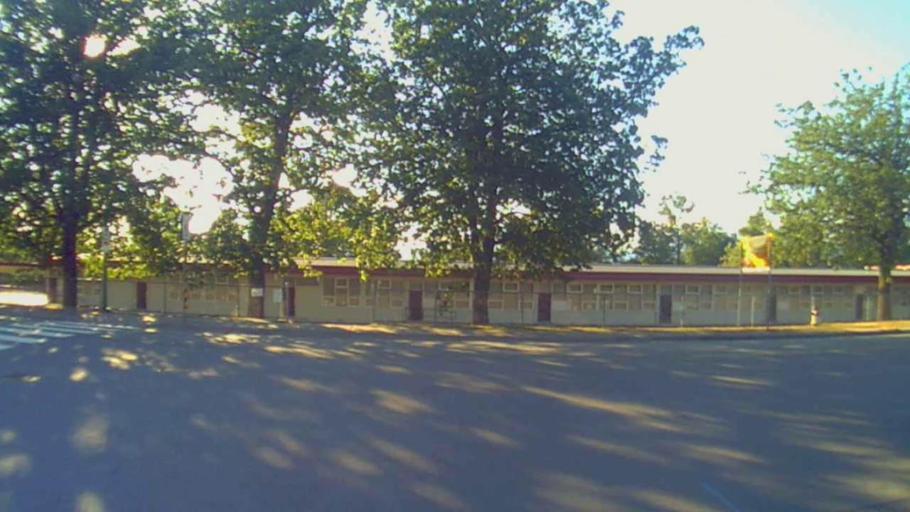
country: CA
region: British Columbia
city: New Westminster
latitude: 49.2333
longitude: -122.9082
